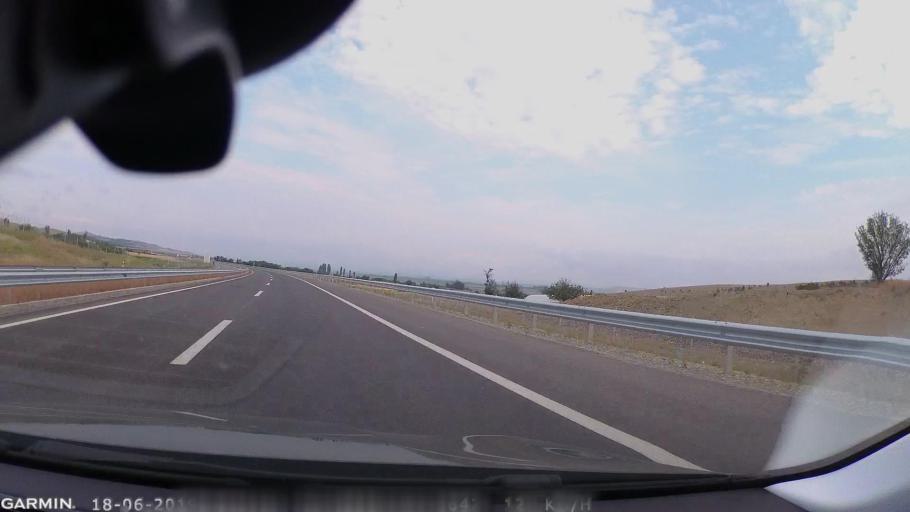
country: MK
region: Stip
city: Shtip
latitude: 41.7873
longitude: 22.1166
